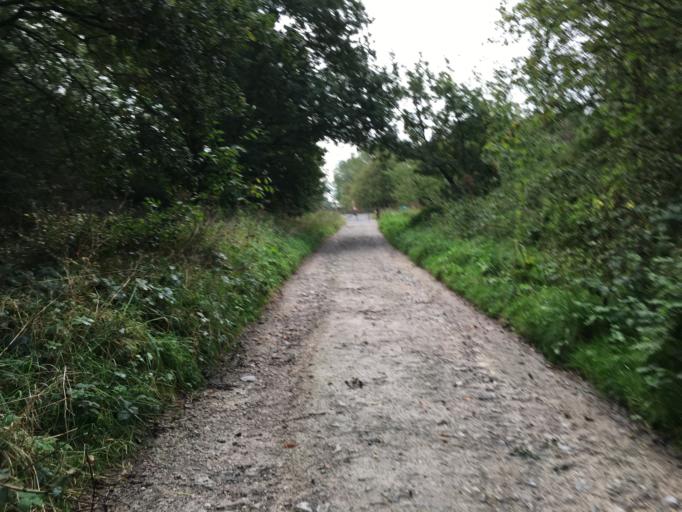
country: GB
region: England
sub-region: North Yorkshire
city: Sleights
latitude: 54.4037
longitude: -0.7230
